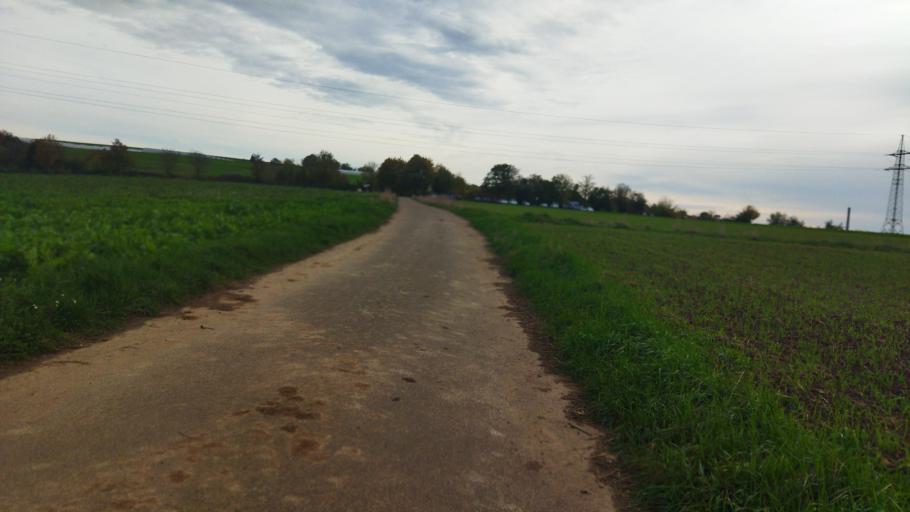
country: DE
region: Baden-Wuerttemberg
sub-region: Regierungsbezirk Stuttgart
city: Gemmrigheim
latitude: 49.0373
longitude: 9.1610
